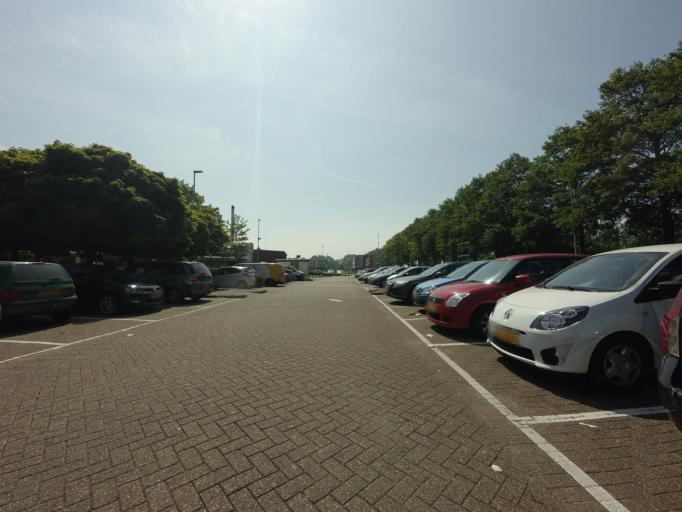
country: NL
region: South Holland
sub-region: Gemeente Hellevoetsluis
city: Hellevoetsluis
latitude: 51.8314
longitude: 4.1452
